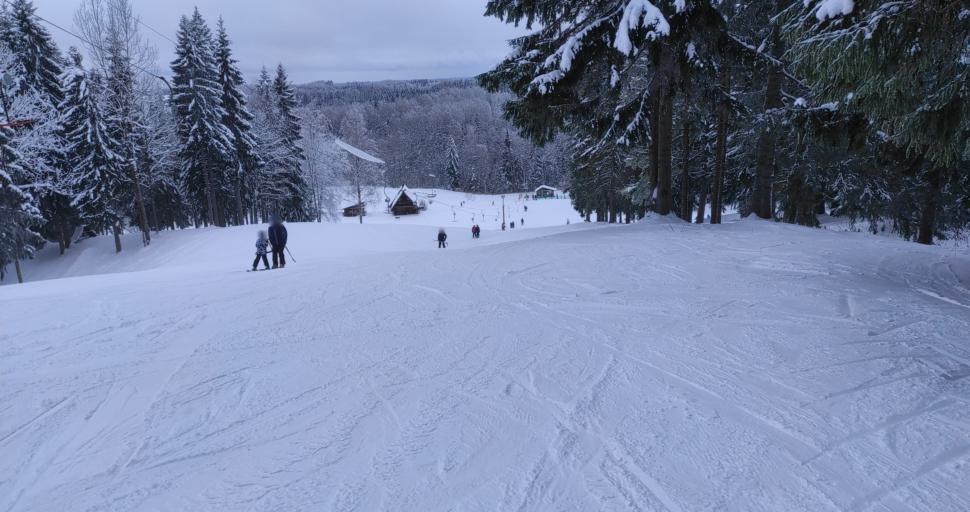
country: LV
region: Vecpiebalga
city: Vecpiebalga
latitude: 56.8737
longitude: 25.9614
